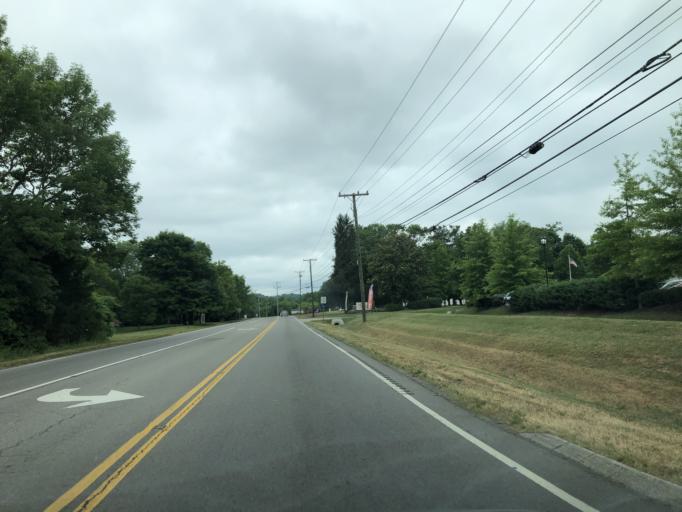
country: US
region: Tennessee
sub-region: Davidson County
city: Goodlettsville
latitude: 36.2797
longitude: -86.7798
